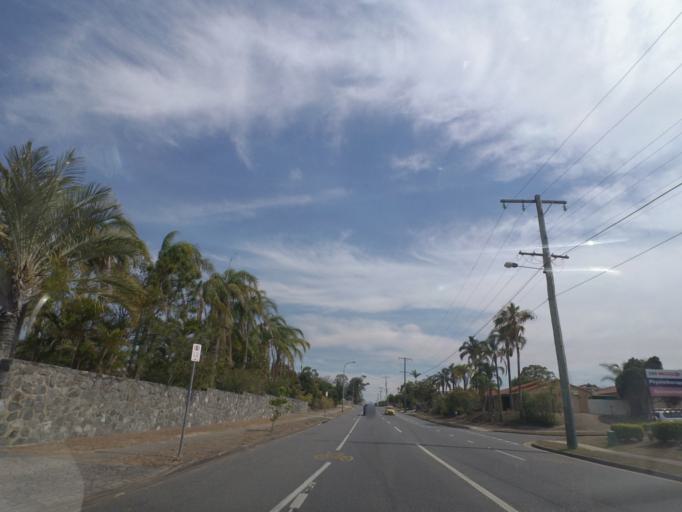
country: AU
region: Queensland
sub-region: Brisbane
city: Sunnybank Hills
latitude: -27.6126
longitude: 153.0618
